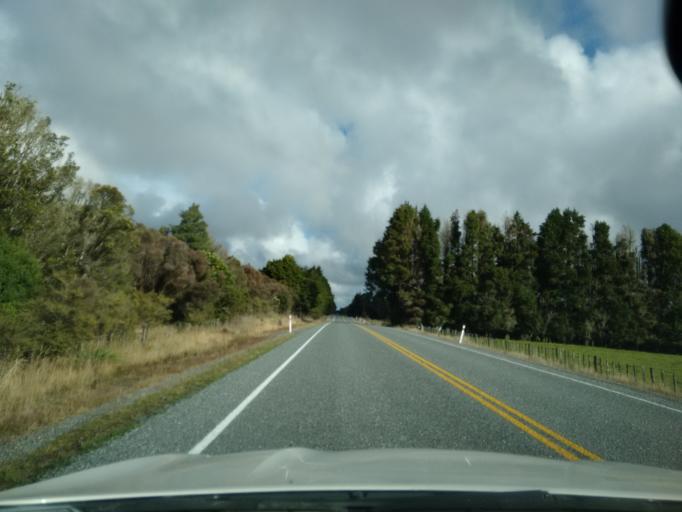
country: NZ
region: Manawatu-Wanganui
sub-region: Ruapehu District
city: Waiouru
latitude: -39.2828
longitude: 175.3864
